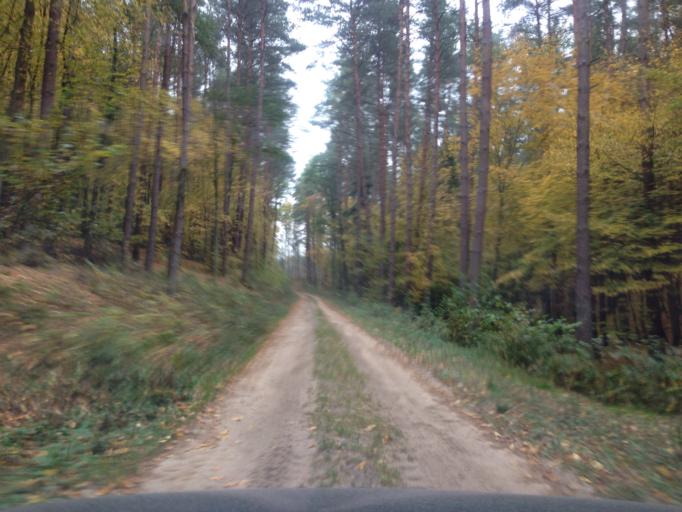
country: PL
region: Warmian-Masurian Voivodeship
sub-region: Powiat dzialdowski
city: Lidzbark
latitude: 53.2683
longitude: 19.7276
